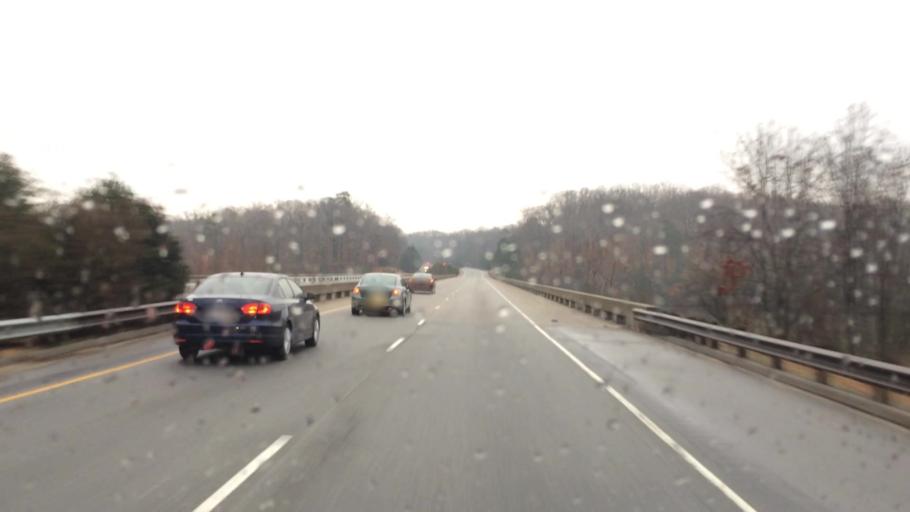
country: US
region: Virginia
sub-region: City of Williamsburg
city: Williamsburg
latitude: 37.2482
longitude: -76.7127
